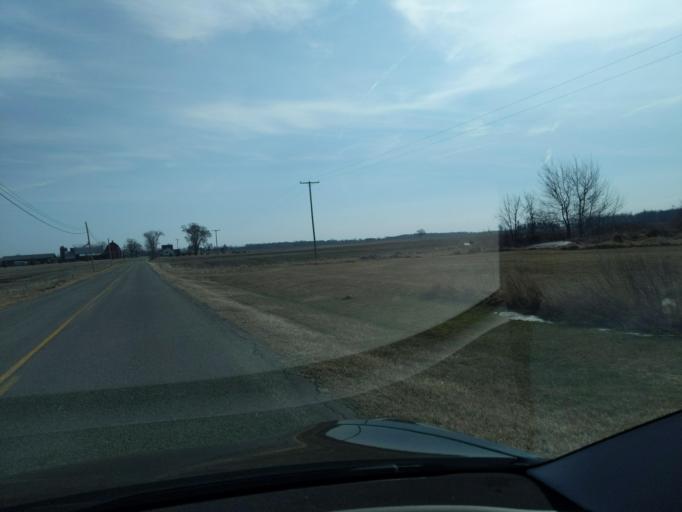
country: US
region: Michigan
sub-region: Ingham County
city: Williamston
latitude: 42.6586
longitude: -84.3246
